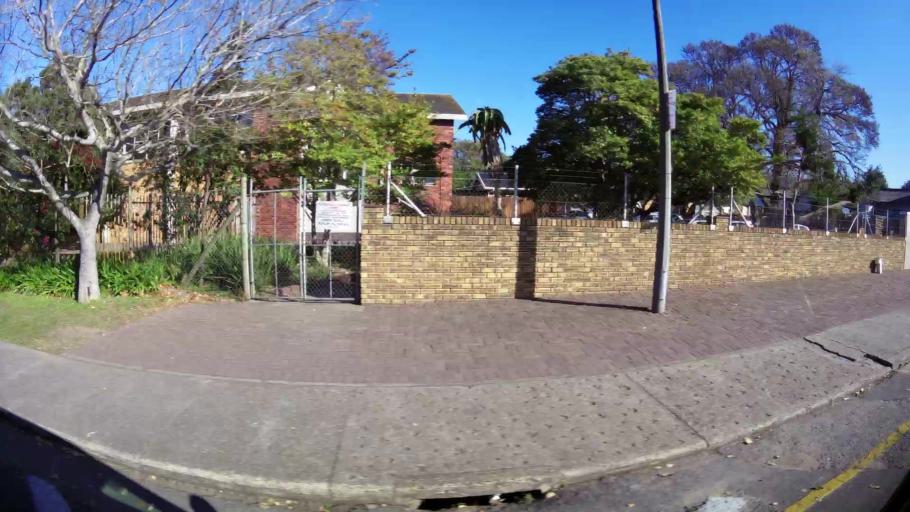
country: ZA
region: Western Cape
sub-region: Eden District Municipality
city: Knysna
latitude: -34.0386
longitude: 23.0488
